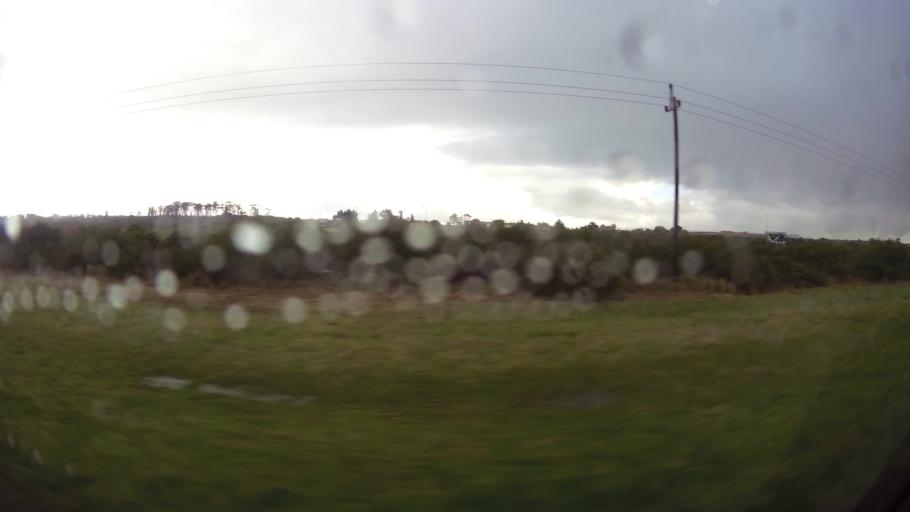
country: ZA
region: Western Cape
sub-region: Eden District Municipality
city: Mossel Bay
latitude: -34.1830
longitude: 22.0921
